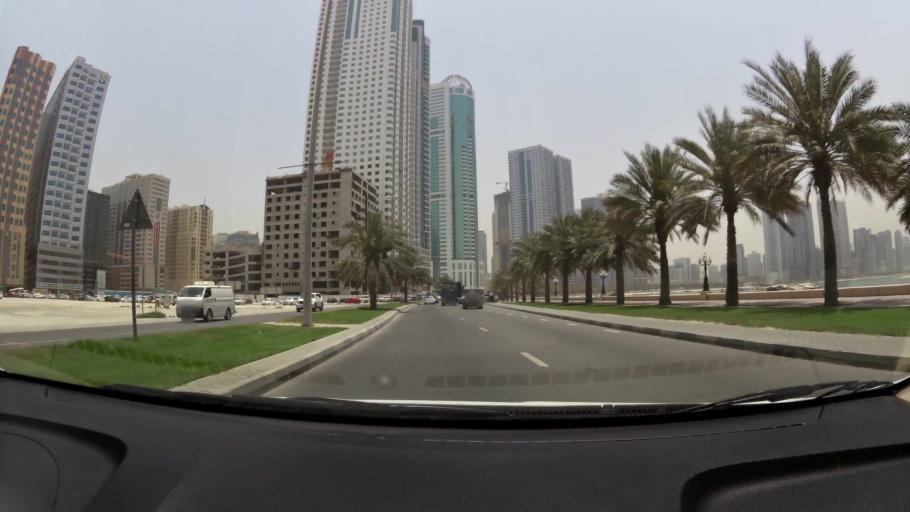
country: AE
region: Ash Shariqah
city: Sharjah
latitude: 25.3268
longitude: 55.3684
